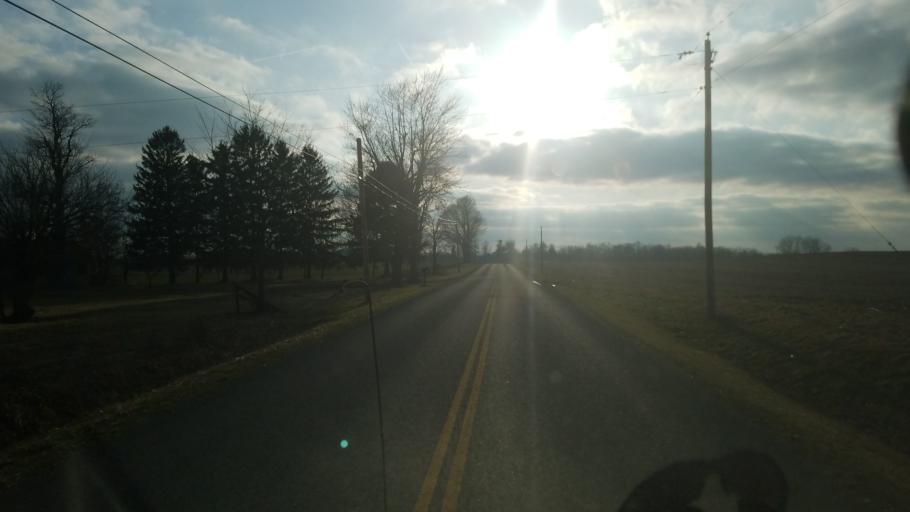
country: US
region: Ohio
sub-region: Logan County
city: West Liberty
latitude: 40.2976
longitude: -83.6776
